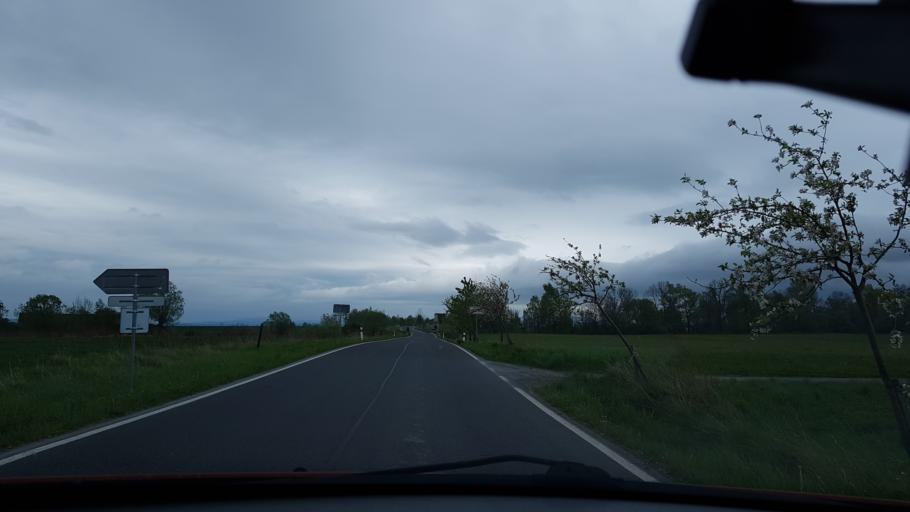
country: PL
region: Opole Voivodeship
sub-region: Powiat nyski
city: Kamienica
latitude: 50.4239
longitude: 16.9668
